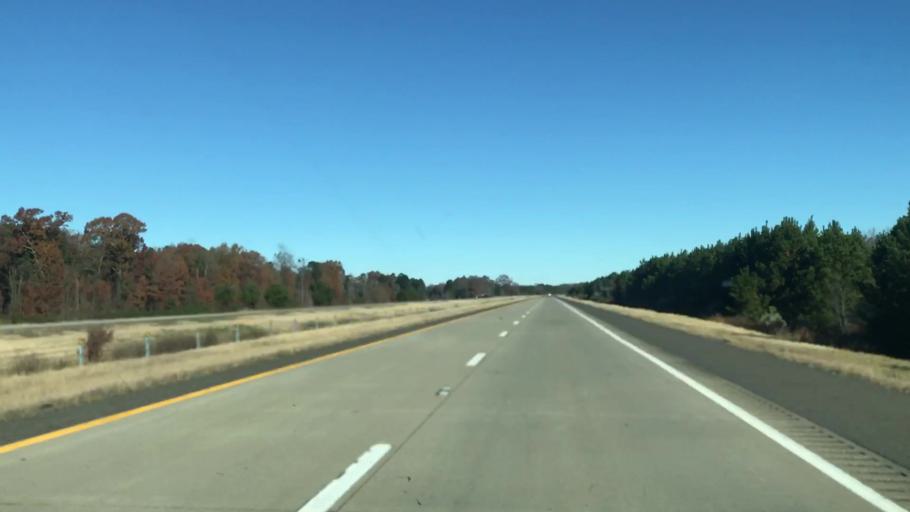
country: US
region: Texas
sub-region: Cass County
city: Queen City
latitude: 33.1915
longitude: -93.8774
